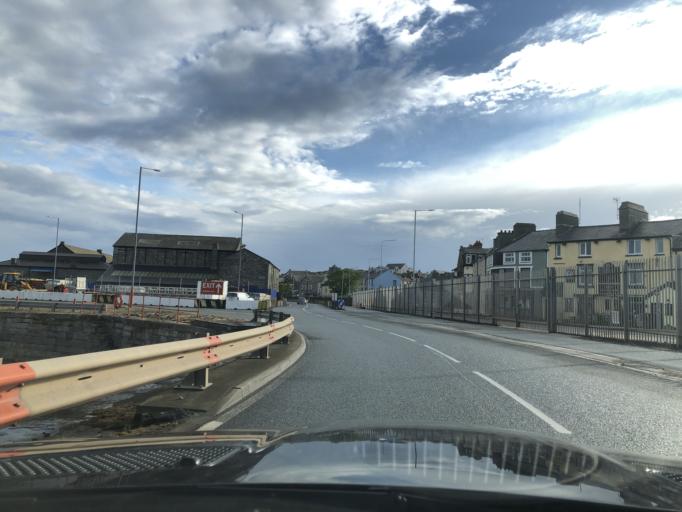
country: GB
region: Wales
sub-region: Anglesey
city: Holyhead
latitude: 53.3137
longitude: -4.6288
